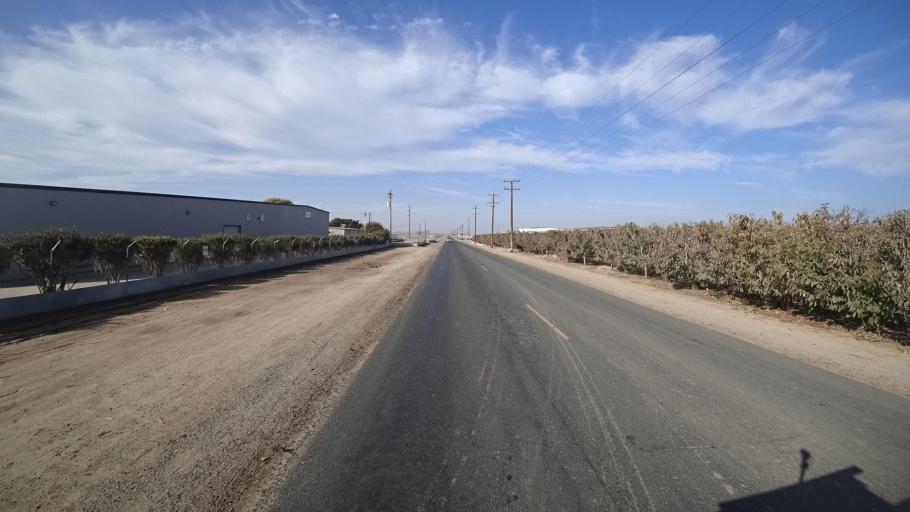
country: US
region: California
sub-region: Kern County
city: McFarland
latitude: 35.6020
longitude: -119.1916
